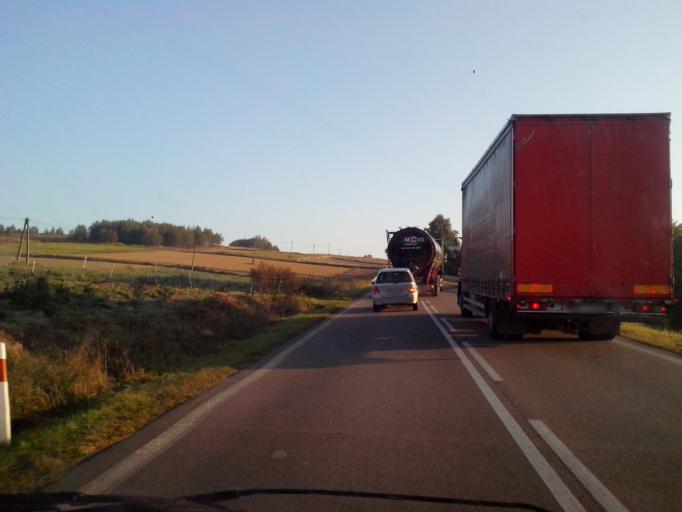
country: PL
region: Subcarpathian Voivodeship
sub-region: Powiat brzozowski
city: Wesola
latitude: 49.8180
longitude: 22.0518
